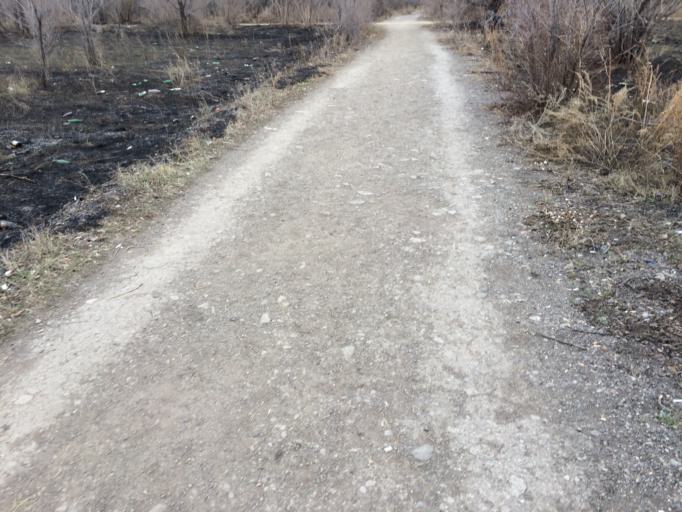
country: RU
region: Chelyabinsk
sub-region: Gorod Magnitogorsk
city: Magnitogorsk
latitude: 53.4414
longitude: 58.9766
